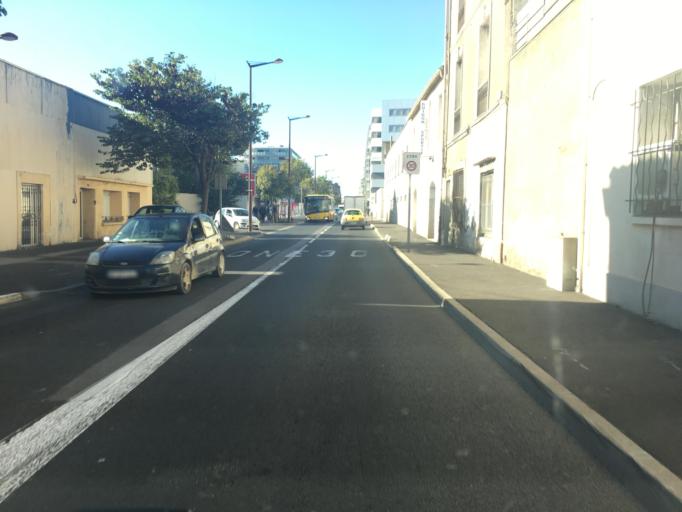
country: FR
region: Languedoc-Roussillon
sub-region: Departement de l'Herault
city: Sete
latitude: 43.4088
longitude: 3.7048
